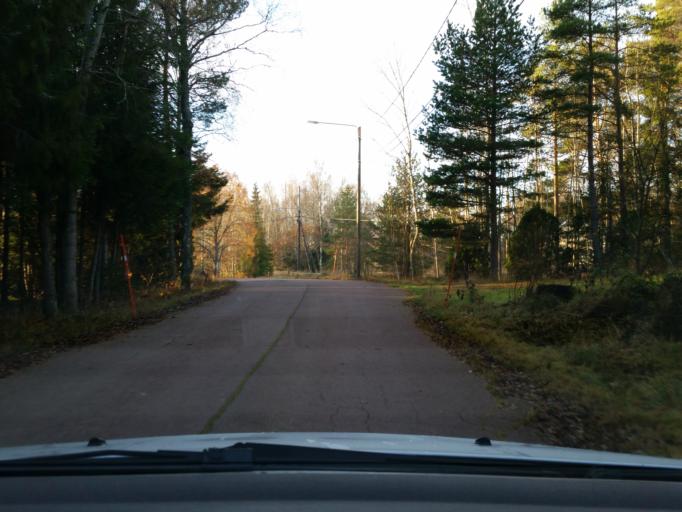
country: AX
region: Alands landsbygd
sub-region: Saltvik
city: Saltvik
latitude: 60.2780
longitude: 20.0676
